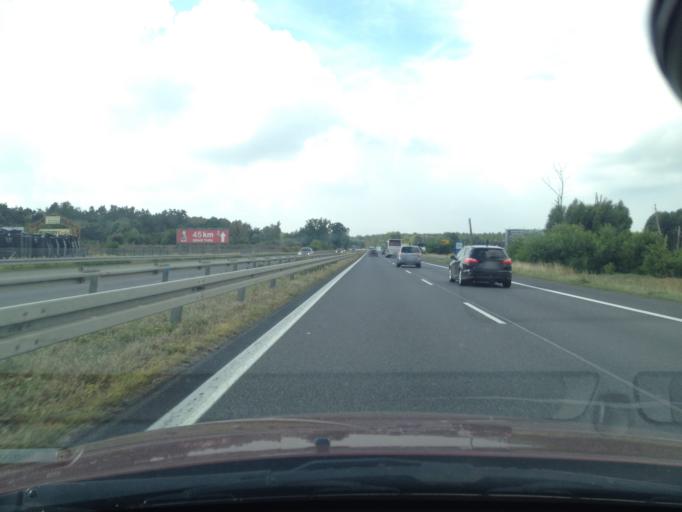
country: PL
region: West Pomeranian Voivodeship
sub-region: Powiat goleniowski
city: Goleniow
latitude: 53.5815
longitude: 14.8113
